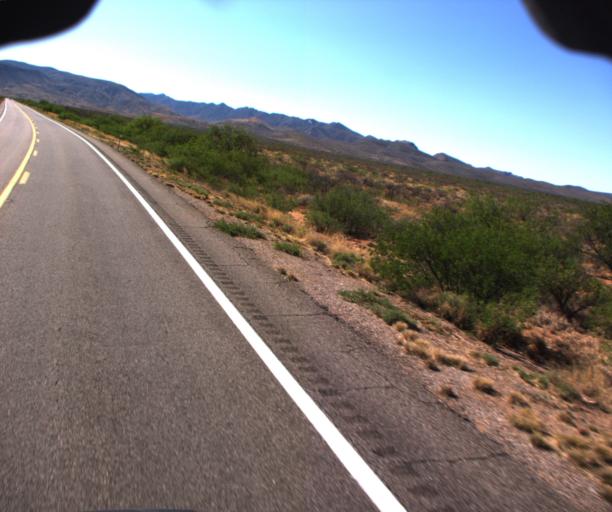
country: US
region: Arizona
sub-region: Cochise County
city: Bisbee
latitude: 31.5654
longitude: -110.0255
